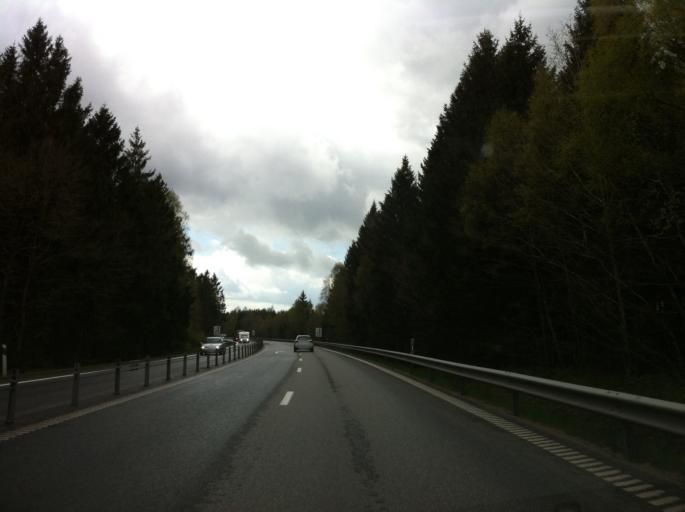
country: SE
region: Skane
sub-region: Hoors Kommun
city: Satofta
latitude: 55.9158
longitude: 13.5294
